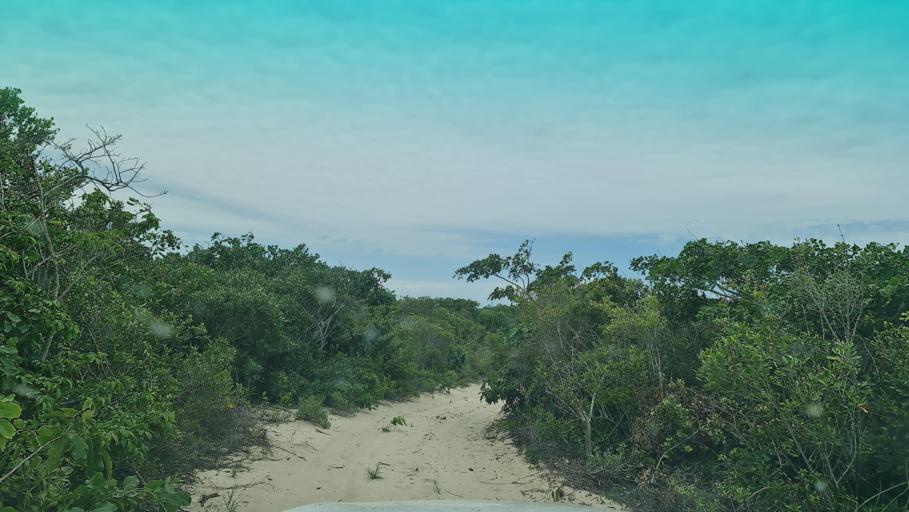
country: MZ
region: Maputo
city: Manhica
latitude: -25.6376
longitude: 32.7836
